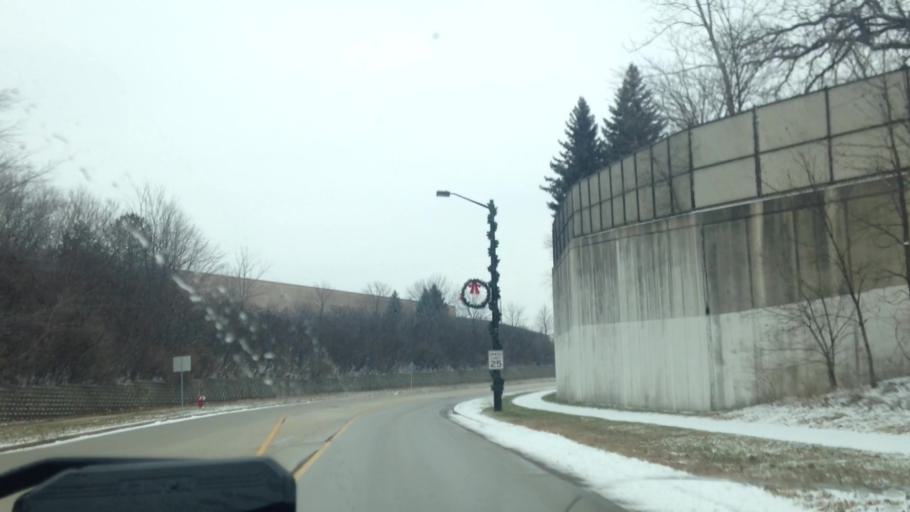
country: US
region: Wisconsin
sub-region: Waukesha County
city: Delafield
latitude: 43.0537
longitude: -88.3761
